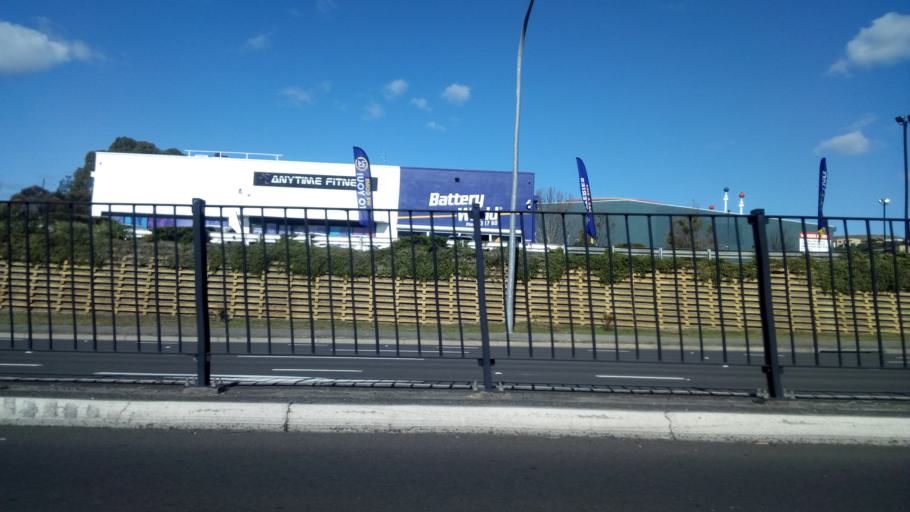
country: AU
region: New South Wales
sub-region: Shellharbour
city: Barrack Heights
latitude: -34.5637
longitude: 150.8307
